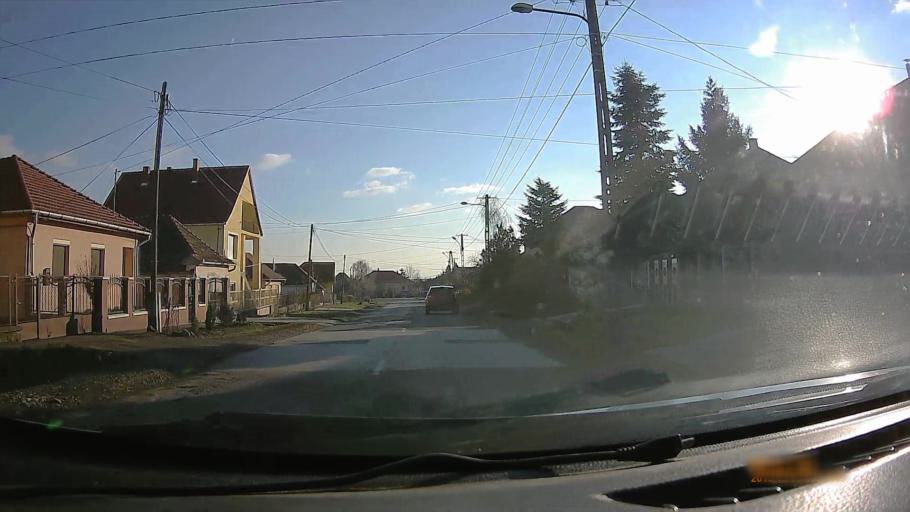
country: HU
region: Heves
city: Domoszlo
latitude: 47.8262
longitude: 20.1117
